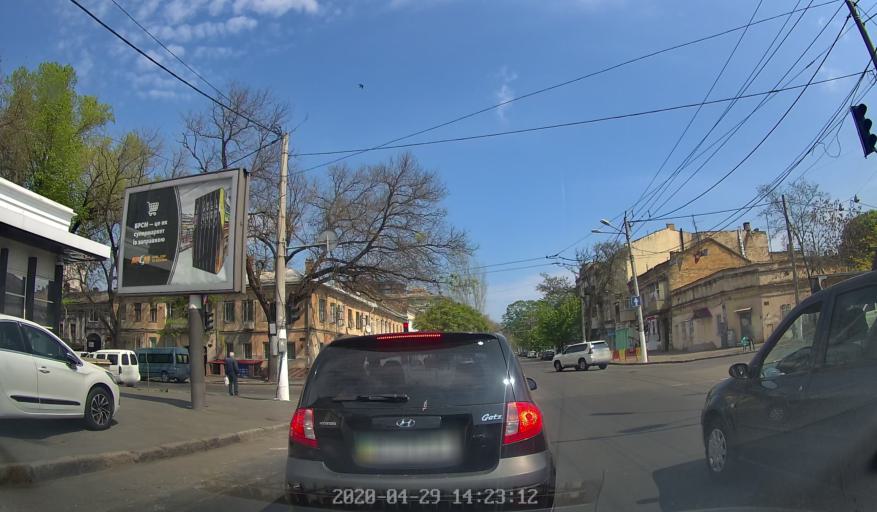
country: NG
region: Niger
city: Lemu
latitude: 9.2942
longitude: 6.1485
